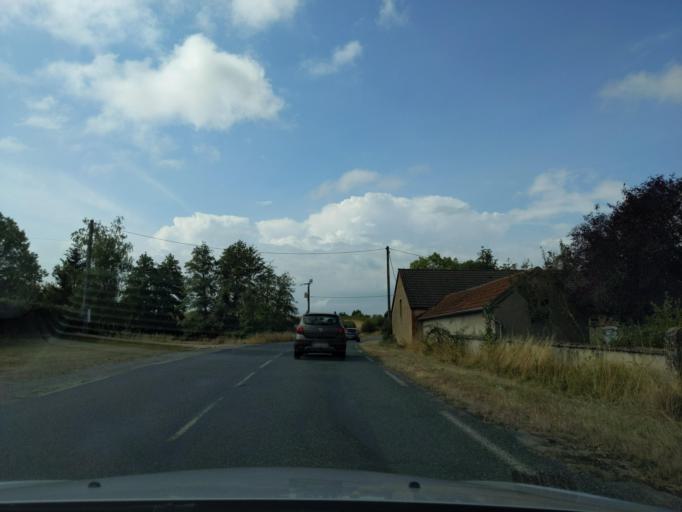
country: FR
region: Bourgogne
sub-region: Departement de Saone-et-Loire
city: Bourbon-Lancy
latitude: 46.6645
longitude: 3.8016
